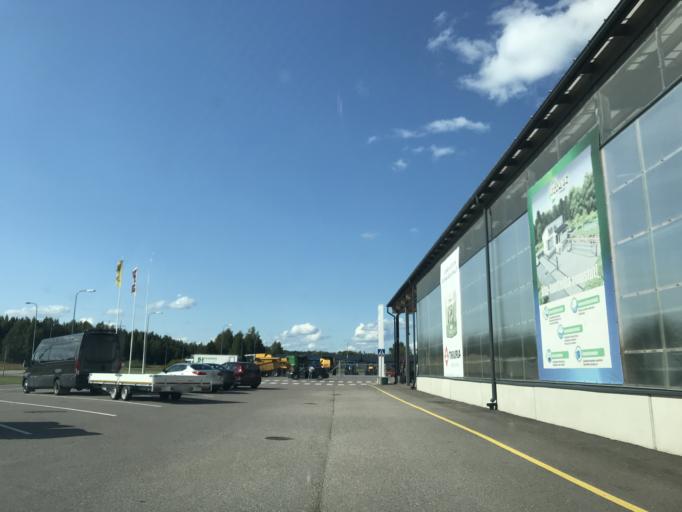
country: FI
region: Uusimaa
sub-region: Helsinki
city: Vihti
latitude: 60.3343
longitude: 24.3350
